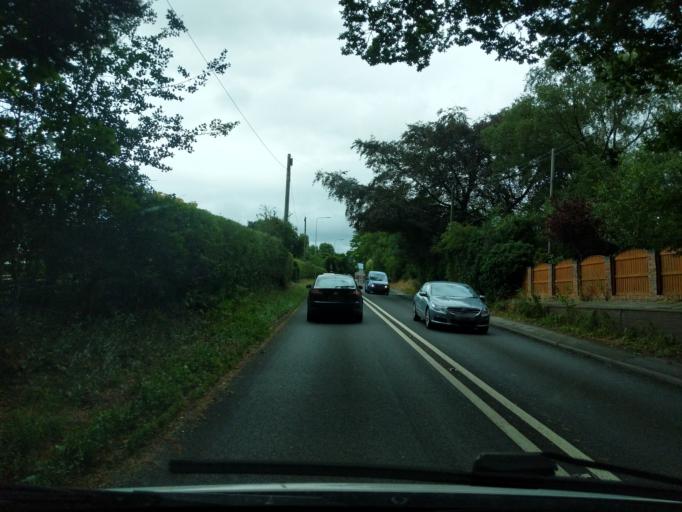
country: GB
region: England
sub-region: Cheshire West and Chester
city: Cuddington
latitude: 53.2380
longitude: -2.6025
